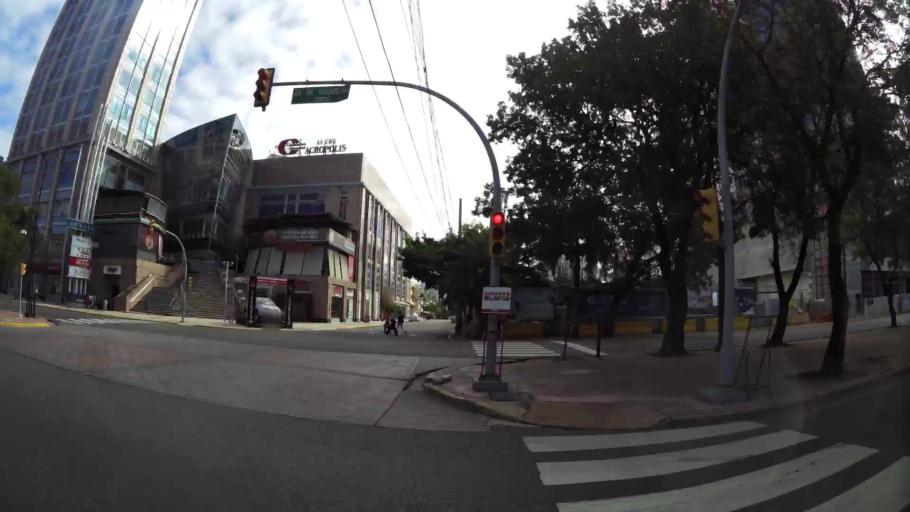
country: DO
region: Nacional
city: La Julia
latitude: 18.4689
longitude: -69.9396
